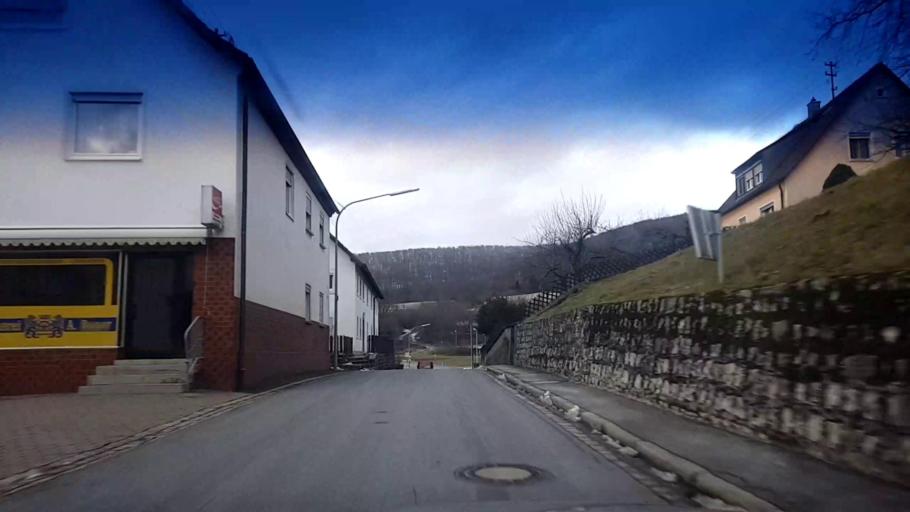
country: DE
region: Bavaria
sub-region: Upper Franconia
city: Litzendorf
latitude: 49.8753
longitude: 11.0664
